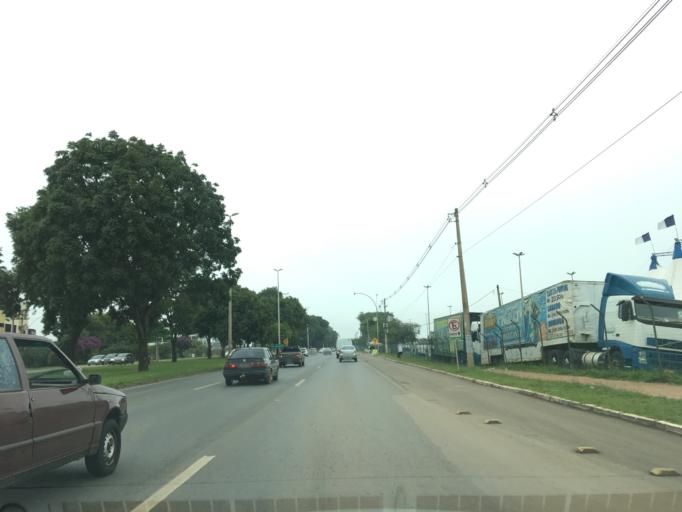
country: BR
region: Federal District
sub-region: Brasilia
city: Brasilia
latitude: -15.8188
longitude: -48.0572
